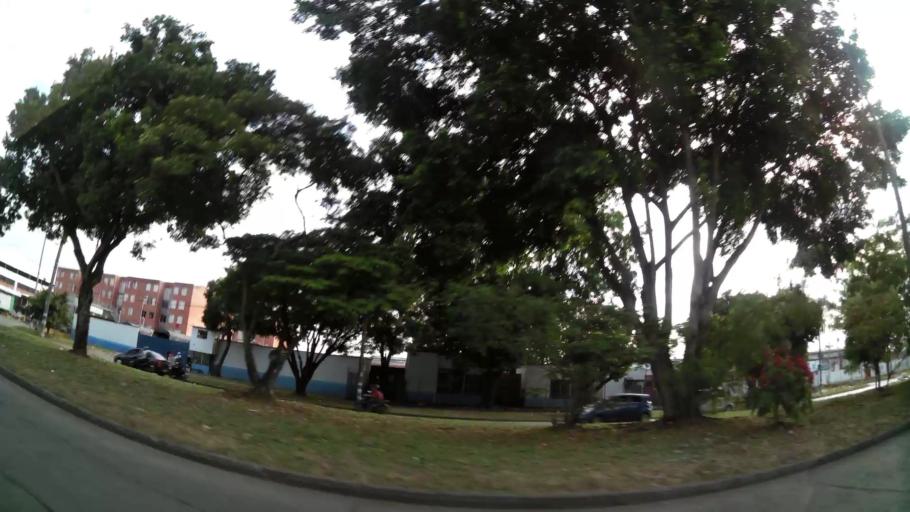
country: CO
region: Valle del Cauca
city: Cali
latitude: 3.4793
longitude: -76.5074
